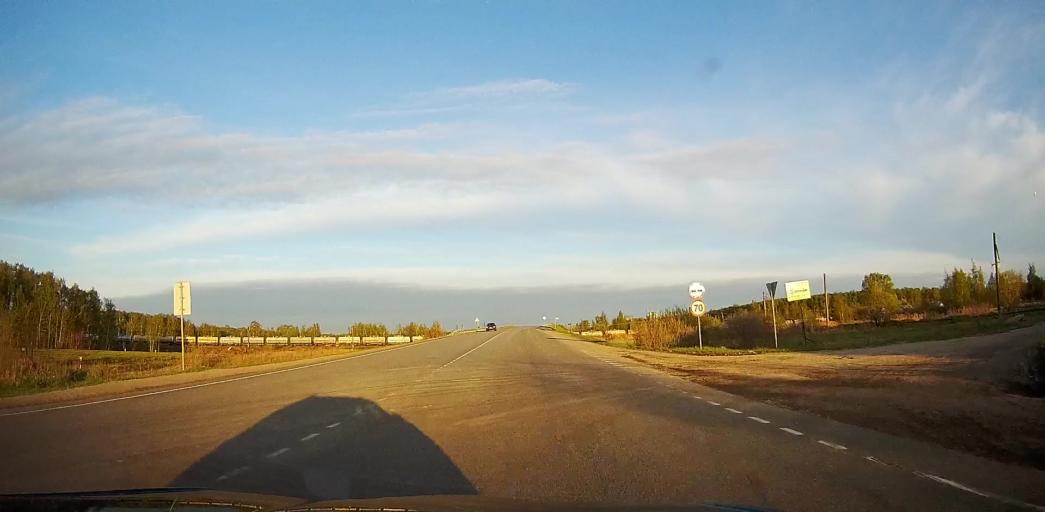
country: RU
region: Moskovskaya
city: Troitskoye
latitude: 55.2191
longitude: 38.5847
